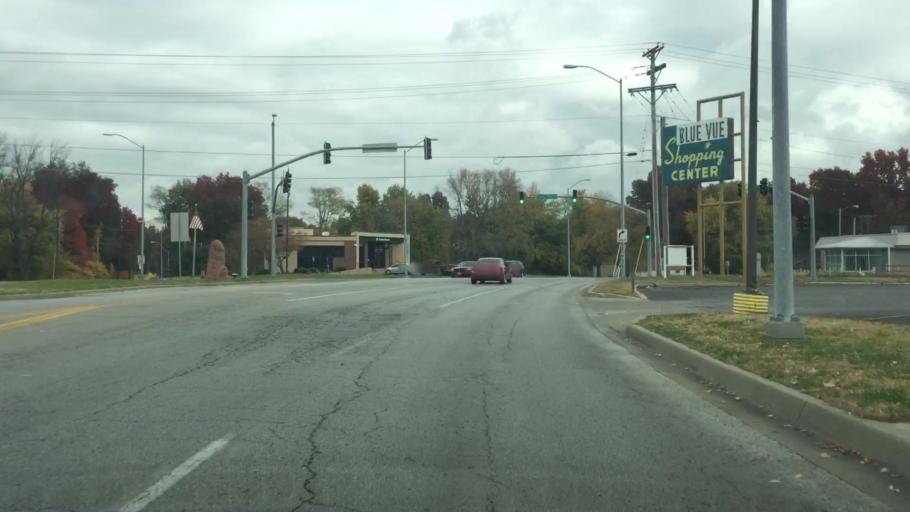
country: US
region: Missouri
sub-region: Jackson County
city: Raytown
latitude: 39.0361
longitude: -94.4388
